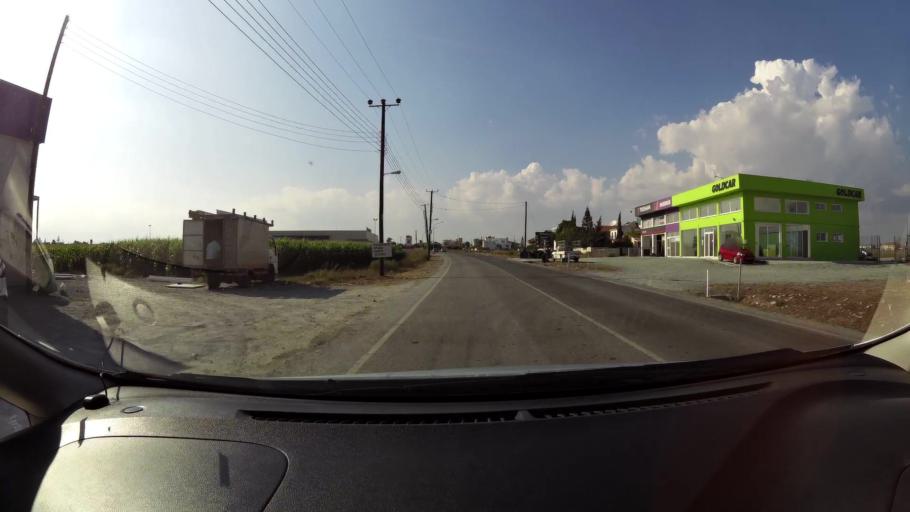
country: CY
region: Larnaka
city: Meneou
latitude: 34.8686
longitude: 33.5963
